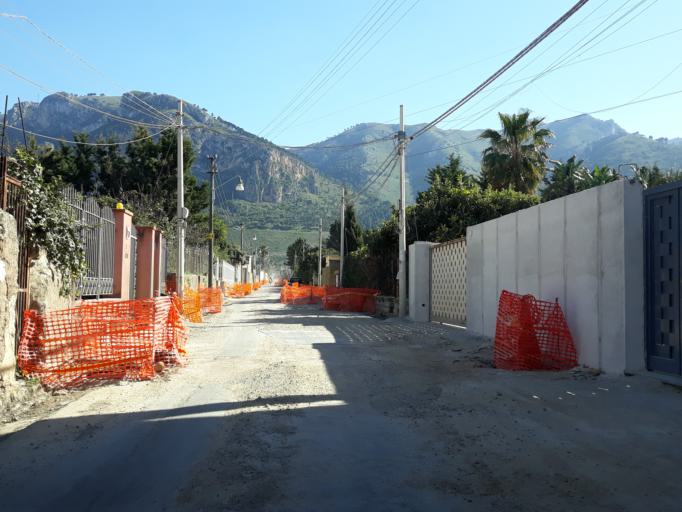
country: IT
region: Sicily
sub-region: Palermo
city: Villa Ciambra
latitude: 38.0841
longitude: 13.3455
